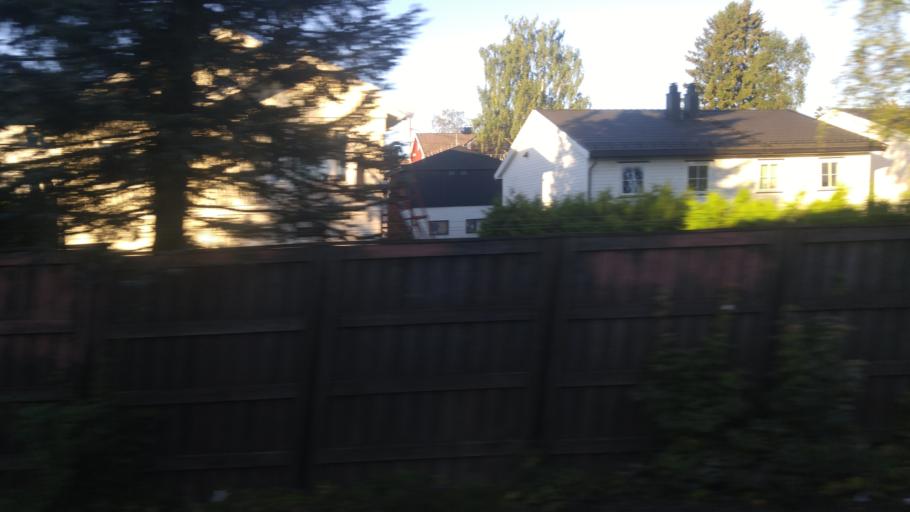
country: NO
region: Akershus
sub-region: Lorenskog
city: Kjenn
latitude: 59.9506
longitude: 10.9108
